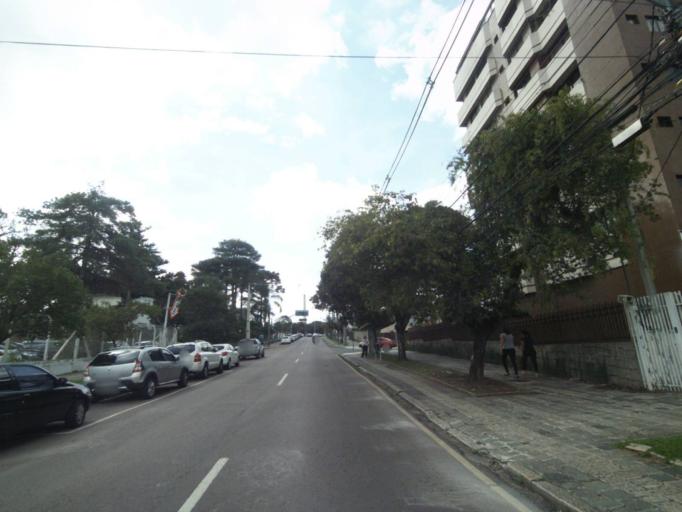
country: BR
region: Parana
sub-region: Curitiba
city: Curitiba
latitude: -25.4223
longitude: -49.2628
